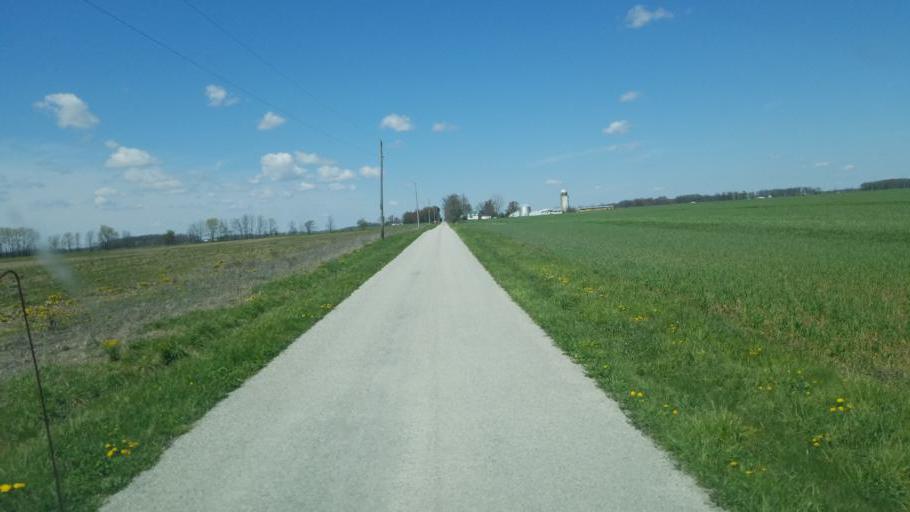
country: US
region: Ohio
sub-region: Marion County
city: Prospect
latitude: 40.3931
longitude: -83.1256
